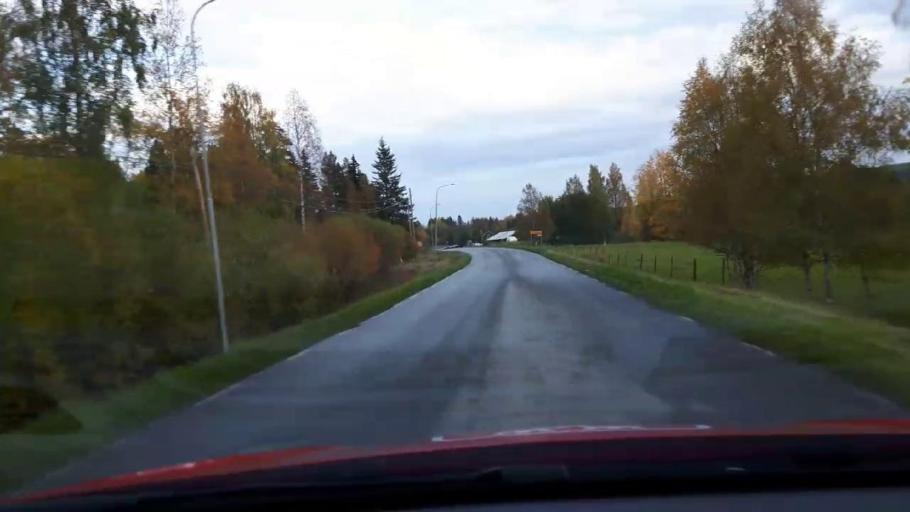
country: SE
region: Jaemtland
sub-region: OEstersunds Kommun
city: Lit
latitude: 63.3201
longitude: 14.8132
